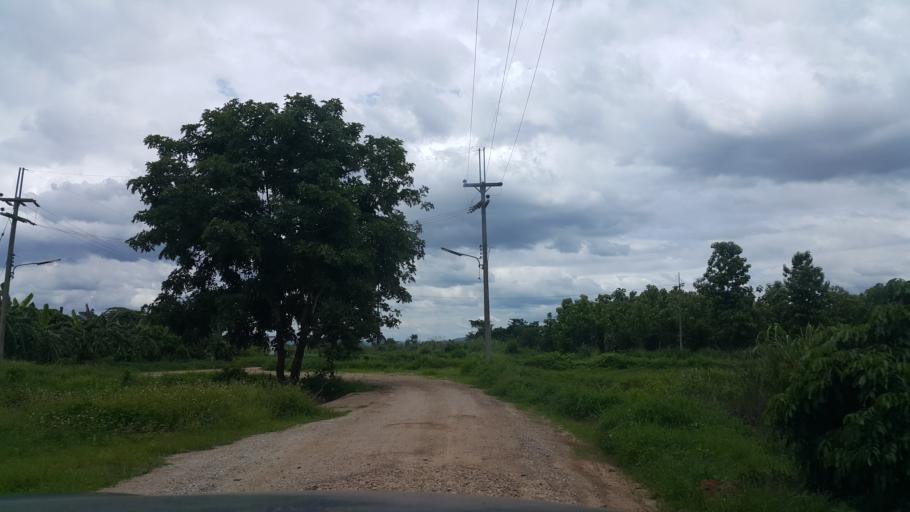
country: TH
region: Chiang Mai
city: Mae Taeng
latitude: 19.1959
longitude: 98.9862
